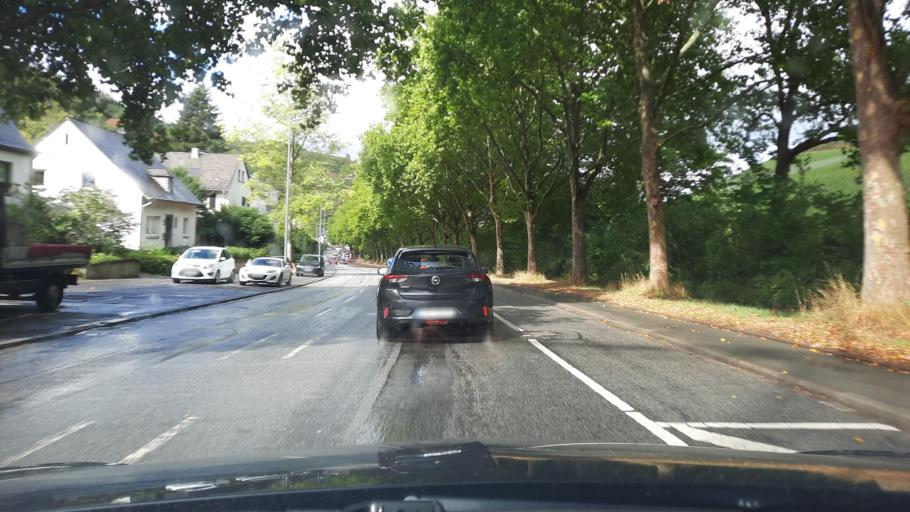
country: DE
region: Rheinland-Pfalz
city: Irsch
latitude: 49.7591
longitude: 6.6792
